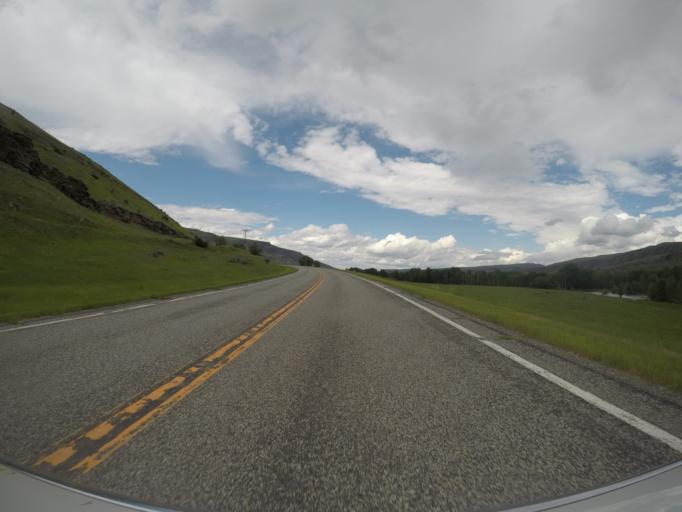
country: US
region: Montana
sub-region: Sweet Grass County
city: Big Timber
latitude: 45.5887
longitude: -110.1787
